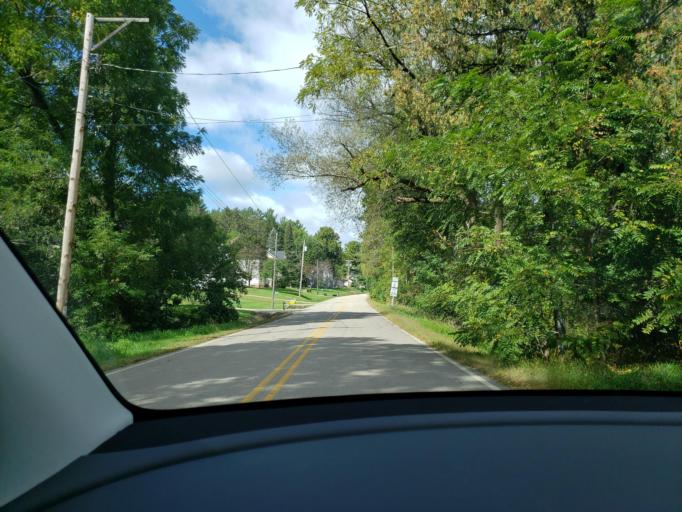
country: US
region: Wisconsin
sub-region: Waupaca County
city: Marion
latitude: 44.7185
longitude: -88.8858
